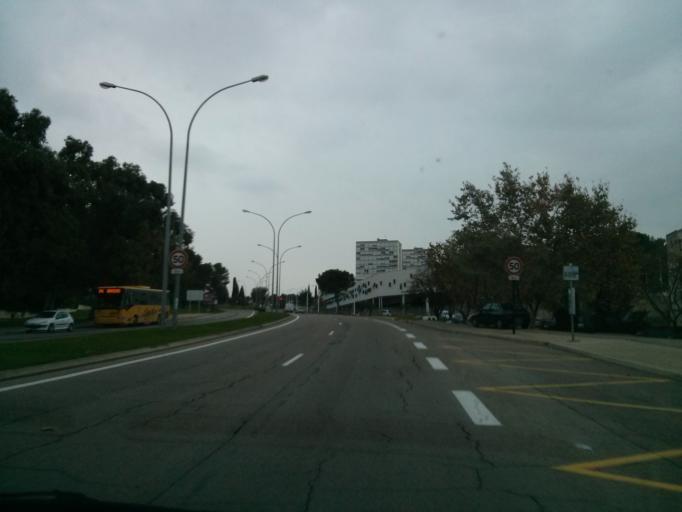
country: FR
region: Languedoc-Roussillon
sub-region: Departement du Gard
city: Nimes
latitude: 43.8238
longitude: 4.3288
